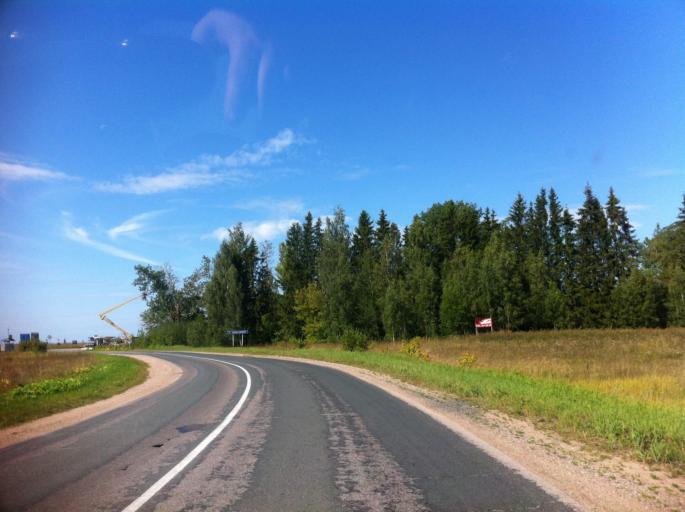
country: RU
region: Pskov
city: Izborsk
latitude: 57.8376
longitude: 27.9912
